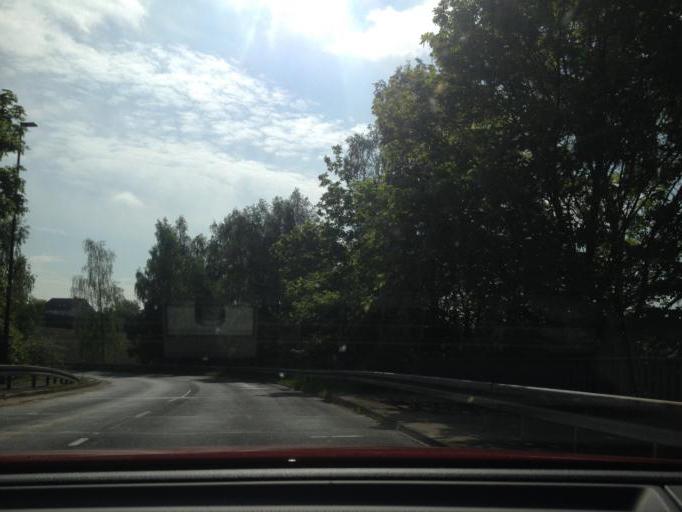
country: DE
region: Bavaria
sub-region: Upper Franconia
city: Marktredwitz
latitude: 50.0181
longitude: 12.1020
